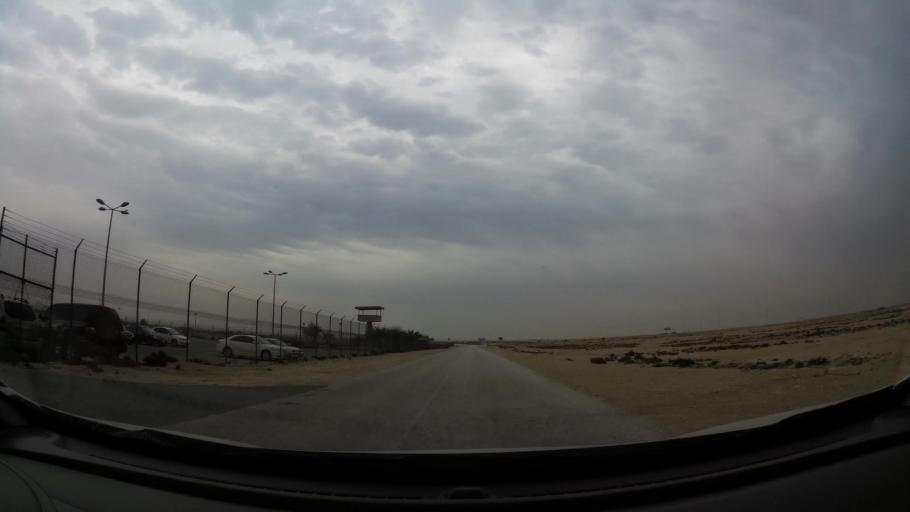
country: BH
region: Central Governorate
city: Dar Kulayb
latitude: 25.8862
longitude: 50.5803
